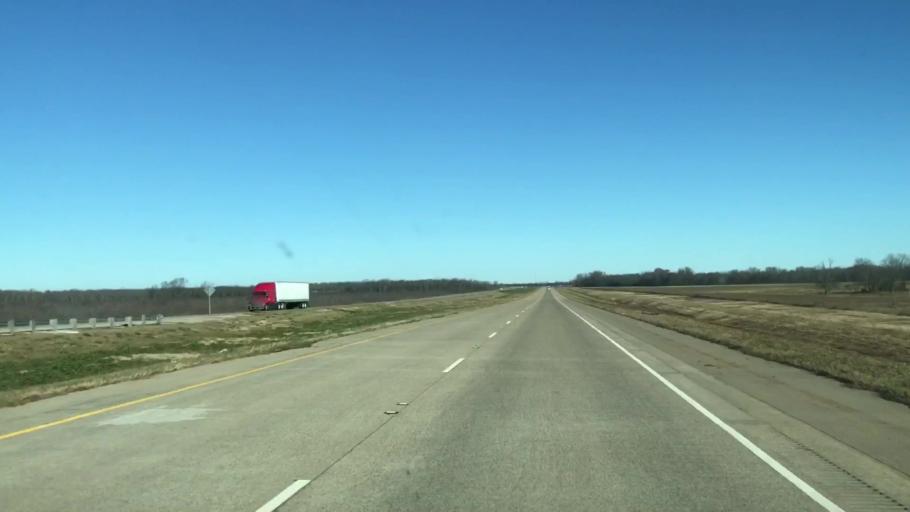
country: US
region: Louisiana
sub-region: Caddo Parish
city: Blanchard
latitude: 32.6313
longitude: -93.8373
